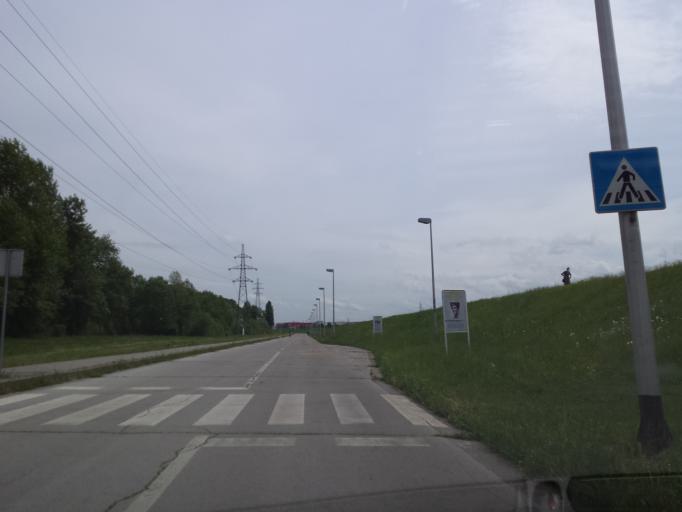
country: HR
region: Grad Zagreb
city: Jankomir
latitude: 45.7764
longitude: 15.9209
